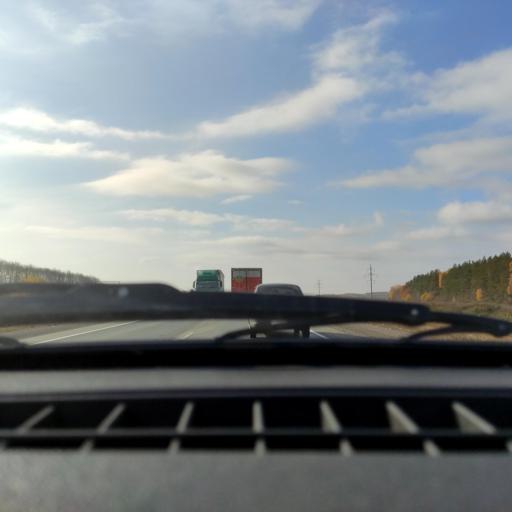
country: RU
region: Bashkortostan
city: Kabakovo
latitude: 54.7154
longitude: 56.2322
